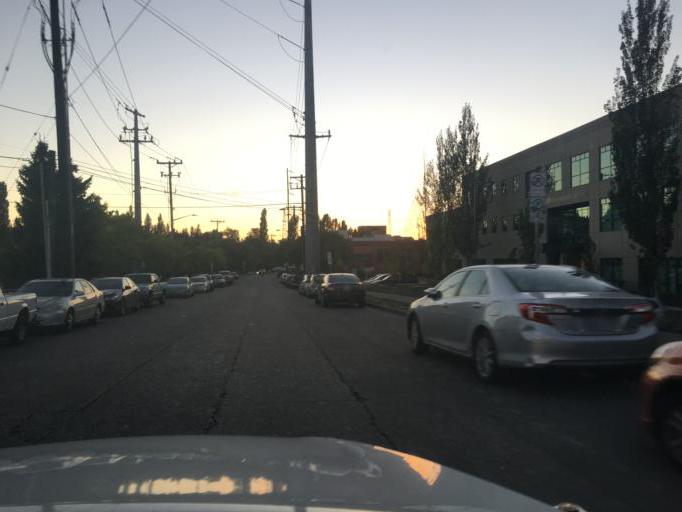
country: US
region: Washington
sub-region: King County
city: Seattle
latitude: 47.6501
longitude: -122.3526
